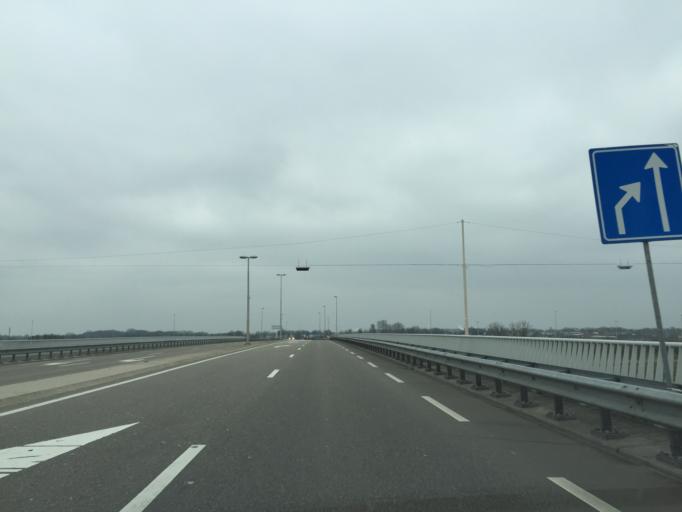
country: NL
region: Utrecht
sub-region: Gemeente Montfoort
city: Montfoort
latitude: 52.0800
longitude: 4.9784
